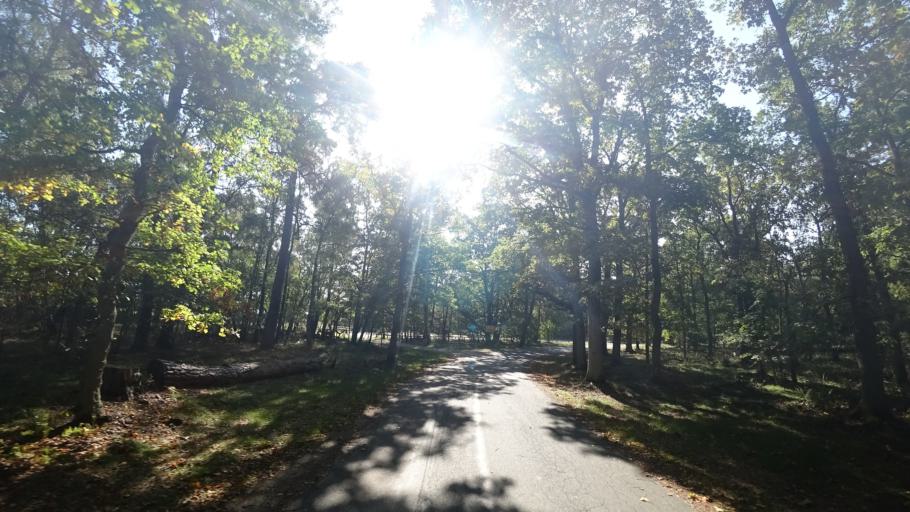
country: SE
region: Skane
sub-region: Kristianstads Kommun
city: Ahus
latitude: 55.9198
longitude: 14.3200
